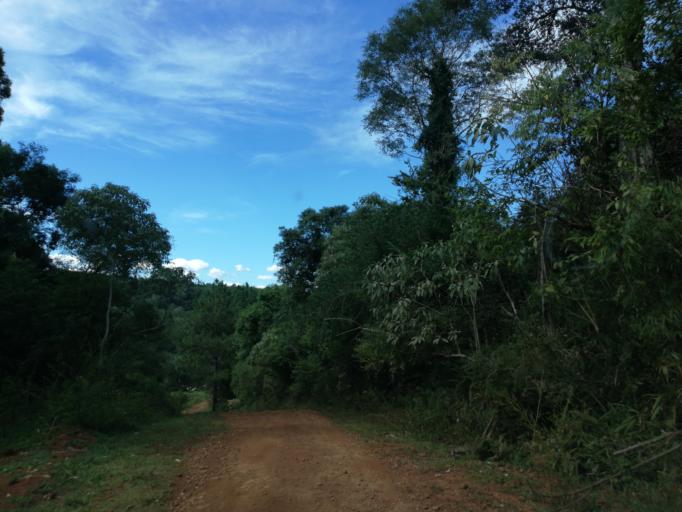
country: AR
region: Misiones
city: Dos de Mayo
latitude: -27.0161
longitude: -54.4164
